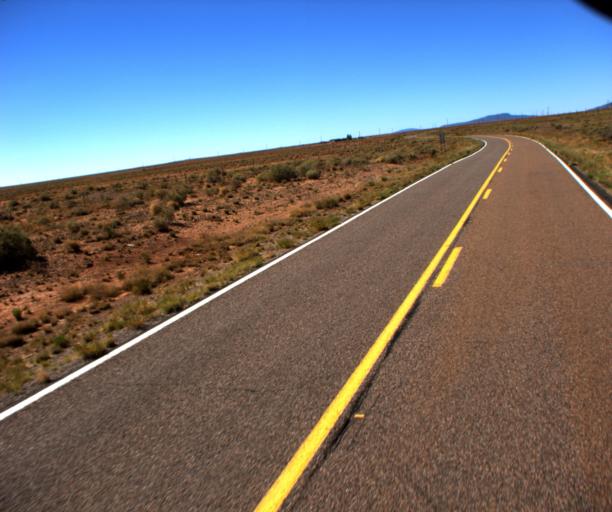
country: US
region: Arizona
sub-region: Coconino County
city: LeChee
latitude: 35.0946
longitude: -110.8606
